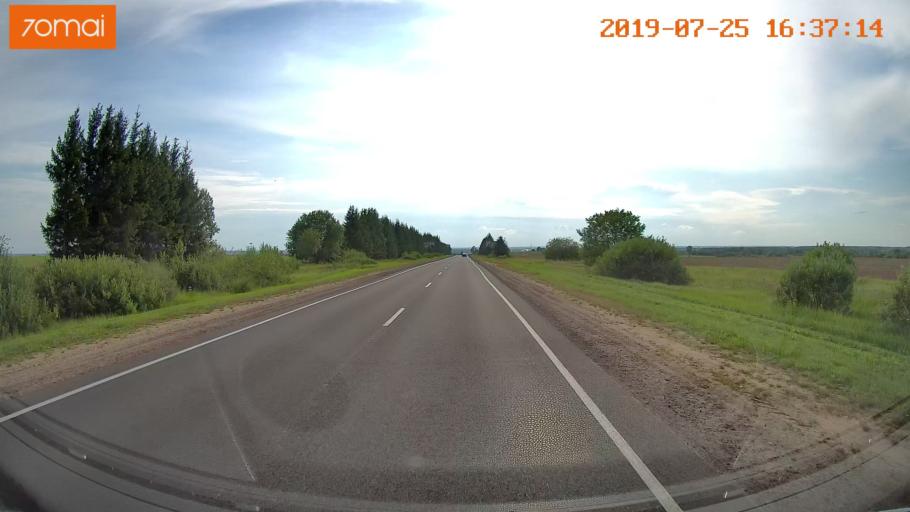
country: RU
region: Ivanovo
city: Privolzhsk
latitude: 57.3912
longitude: 41.3817
